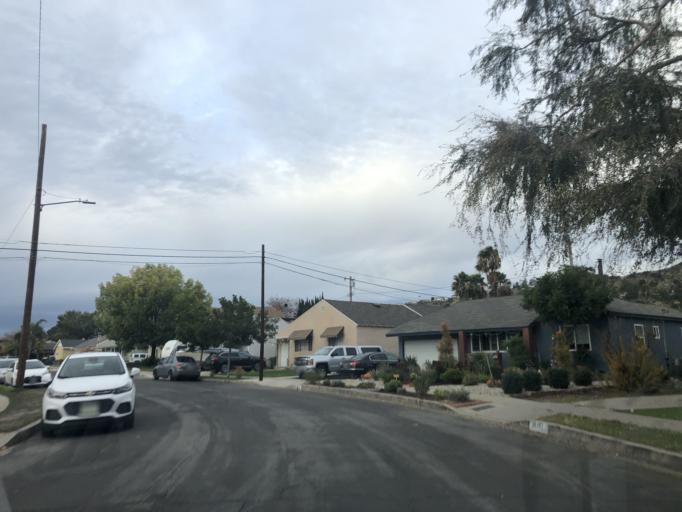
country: US
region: California
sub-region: Los Angeles County
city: North Hollywood
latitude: 34.2109
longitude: -118.3506
